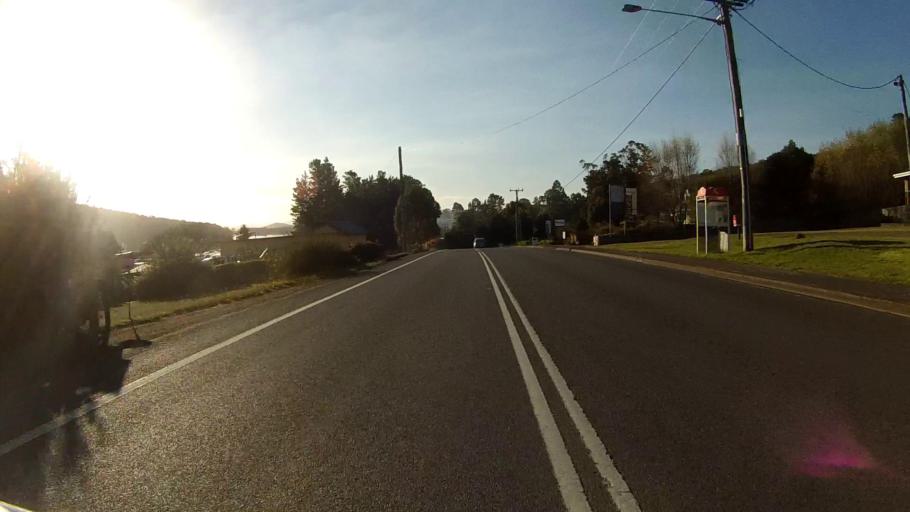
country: AU
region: Tasmania
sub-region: Clarence
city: Sandford
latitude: -43.0558
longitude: 147.8652
